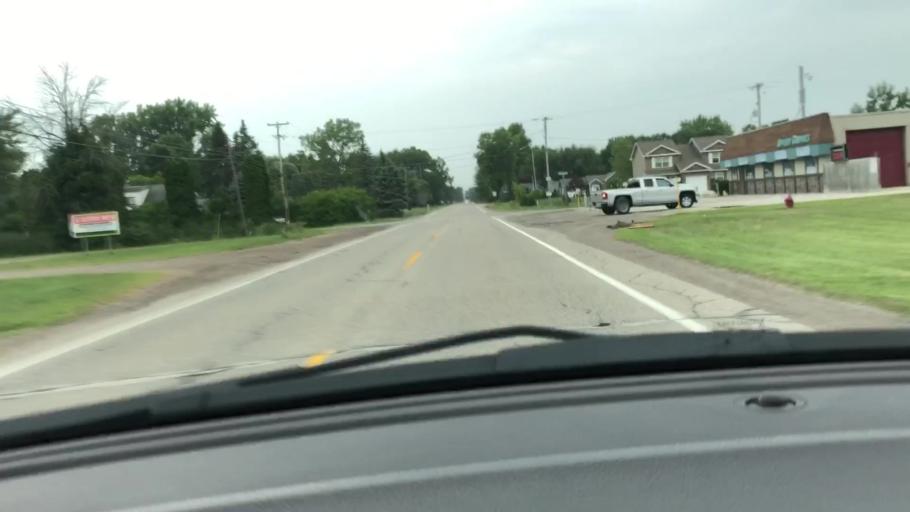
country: US
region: Michigan
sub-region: Bay County
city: Auburn
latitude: 43.6043
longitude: -84.1277
